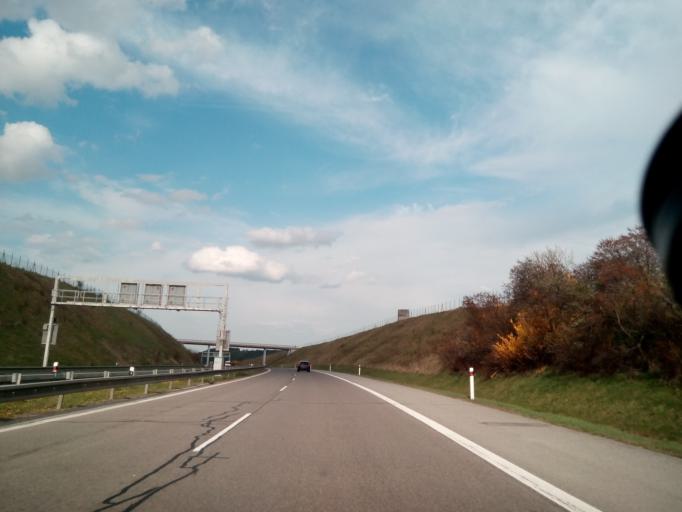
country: SK
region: Kosicky
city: Krompachy
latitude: 48.9970
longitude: 20.9229
